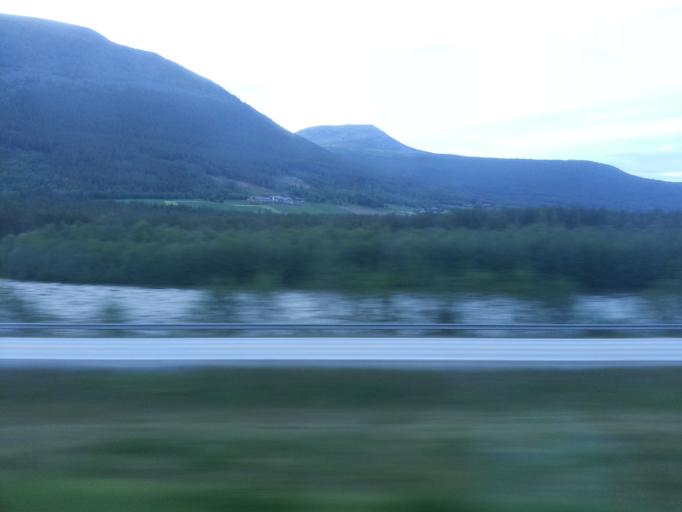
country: NO
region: Oppland
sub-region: Dovre
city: Dovre
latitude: 61.9338
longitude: 9.3038
